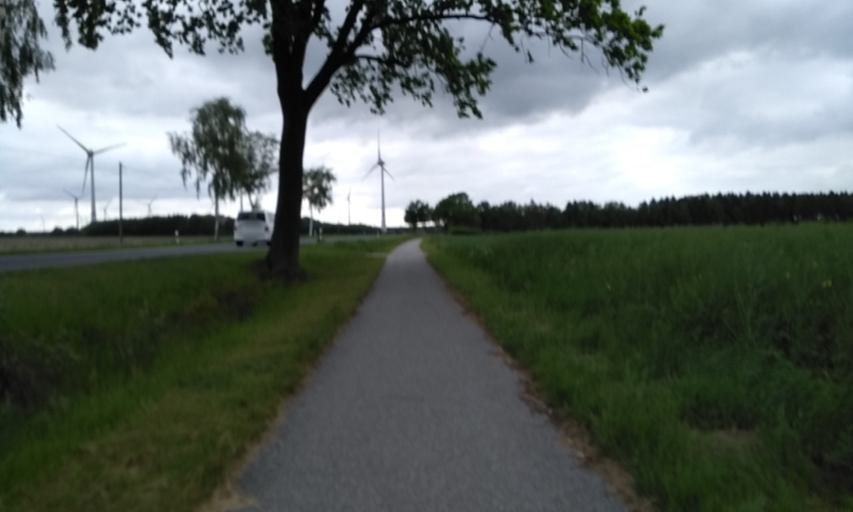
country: DE
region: Lower Saxony
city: Harsefeld
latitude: 53.4824
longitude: 9.4927
